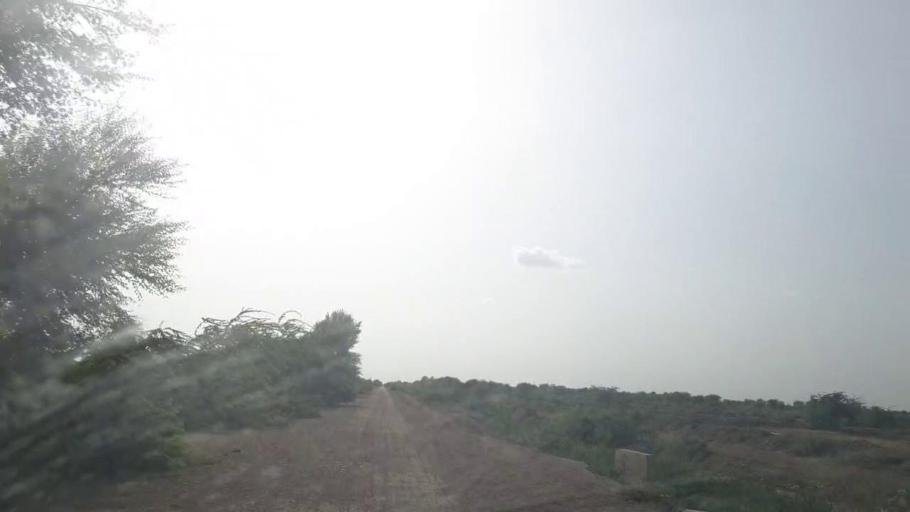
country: PK
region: Sindh
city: Tando Bago
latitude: 24.8247
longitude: 69.1248
